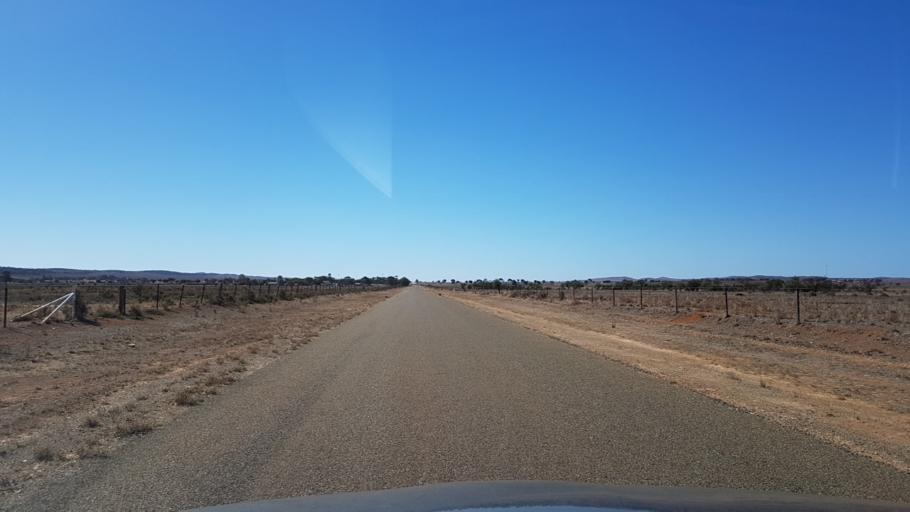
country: AU
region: South Australia
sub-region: Peterborough
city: Peterborough
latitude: -32.9820
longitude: 138.8515
